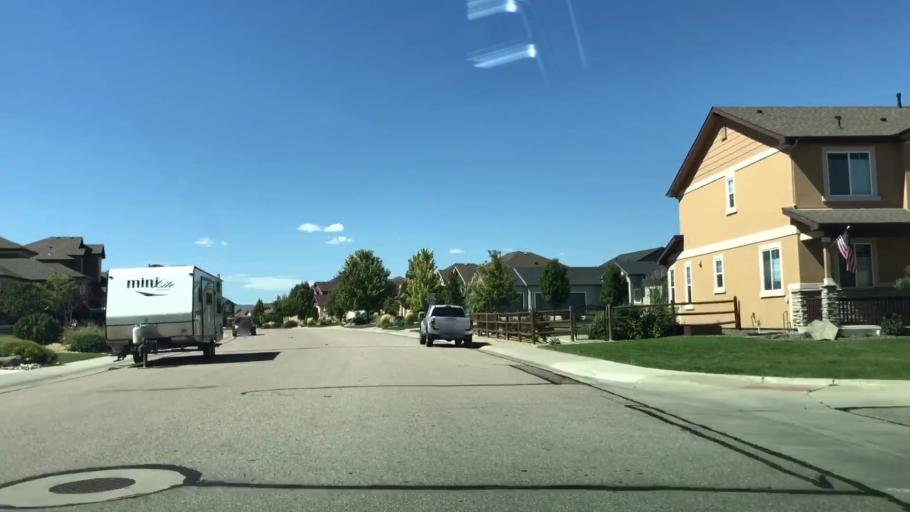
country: US
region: Colorado
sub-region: Weld County
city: Windsor
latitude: 40.4554
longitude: -104.9506
